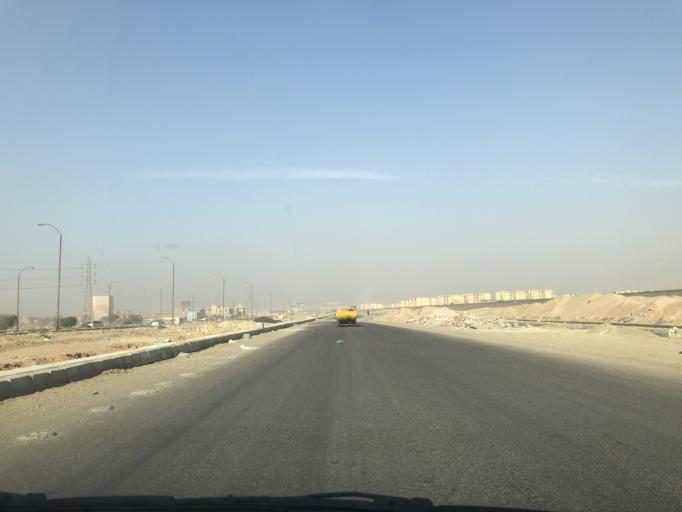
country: EG
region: Al Jizah
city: Madinat Sittah Uktubar
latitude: 29.8994
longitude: 30.9066
